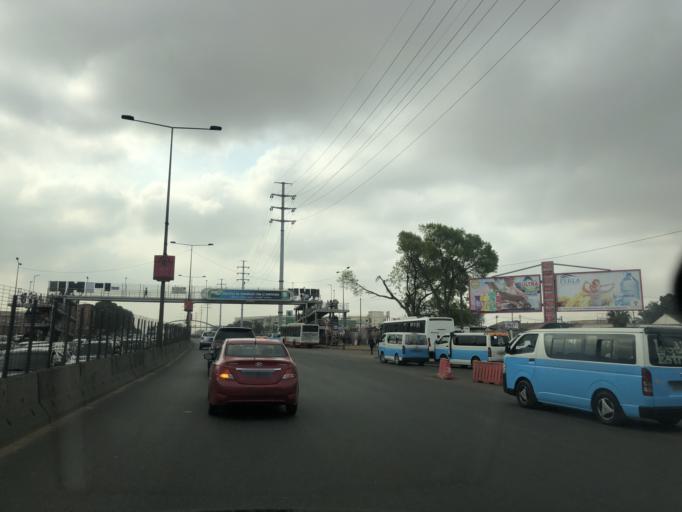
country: AO
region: Luanda
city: Luanda
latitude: -8.8371
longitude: 13.2607
